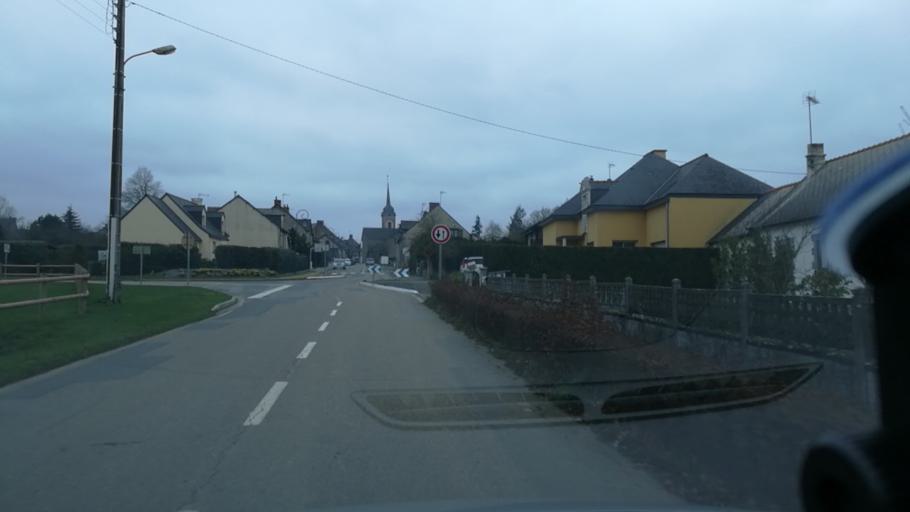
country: FR
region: Brittany
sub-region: Departement d'Ille-et-Vilaine
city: Tresboeuf
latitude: 47.8829
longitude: -1.5422
